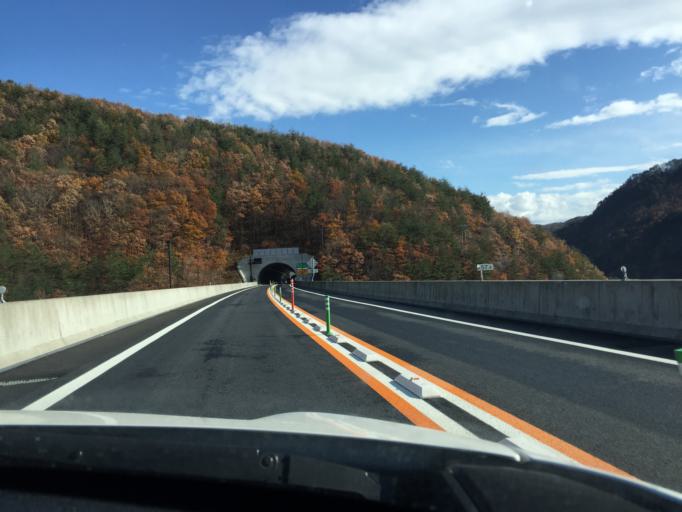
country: JP
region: Fukushima
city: Fukushima-shi
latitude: 37.8415
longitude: 140.3681
